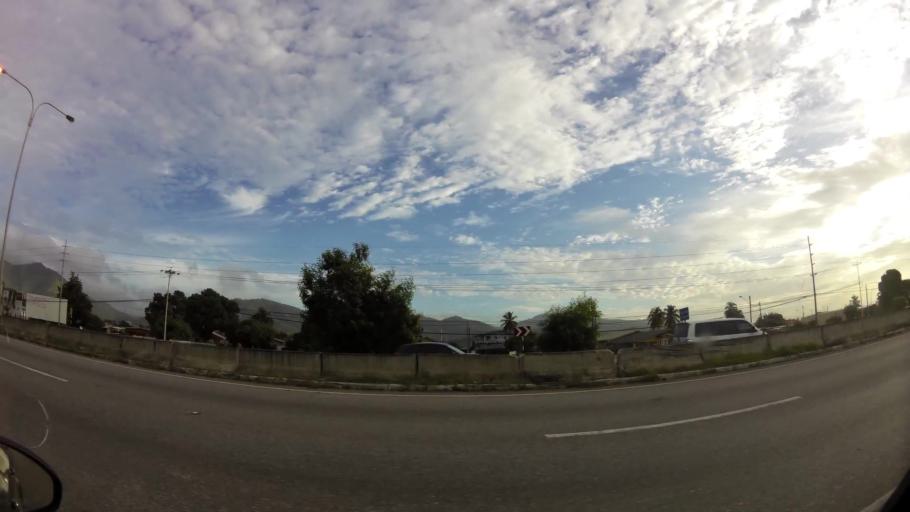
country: TT
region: Tunapuna/Piarco
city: Paradise
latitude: 10.6327
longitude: -61.3627
